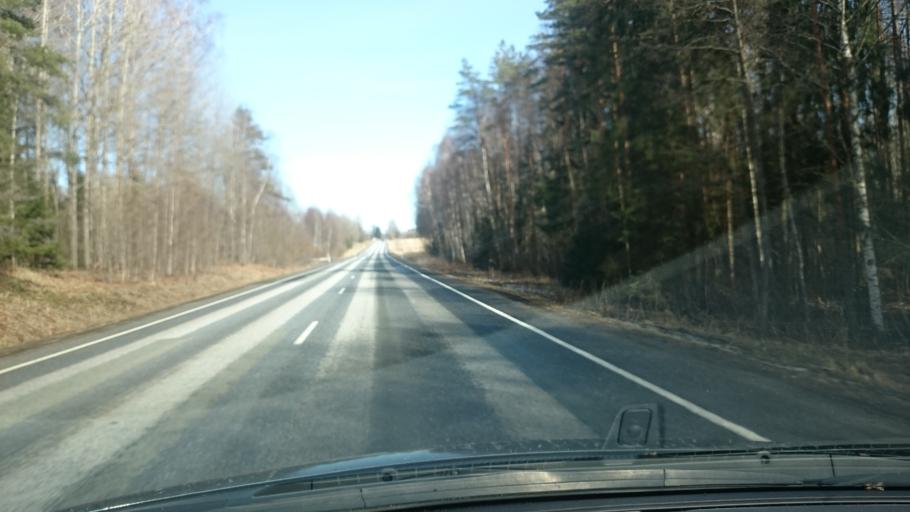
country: EE
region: Jaervamaa
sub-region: Tueri vald
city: Sarevere
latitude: 58.7454
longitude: 25.3106
